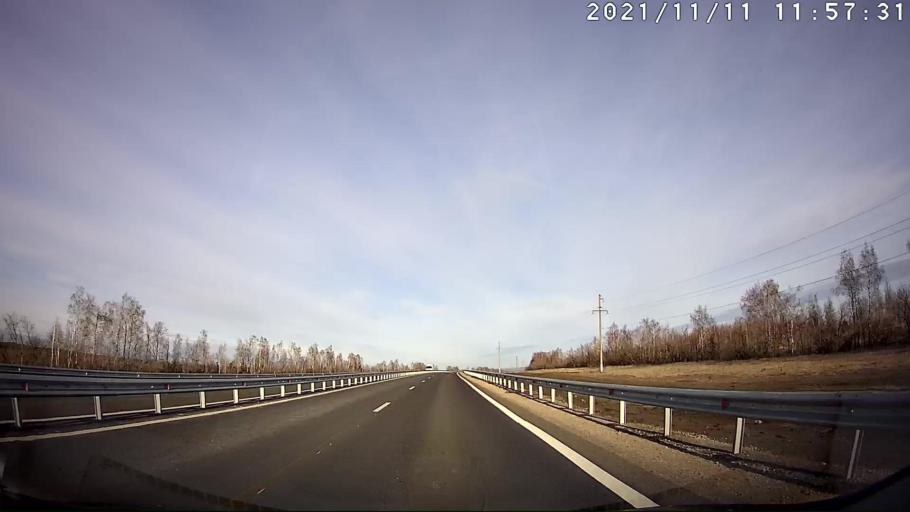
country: RU
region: Samara
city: Balasheyka
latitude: 53.5673
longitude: 48.3294
